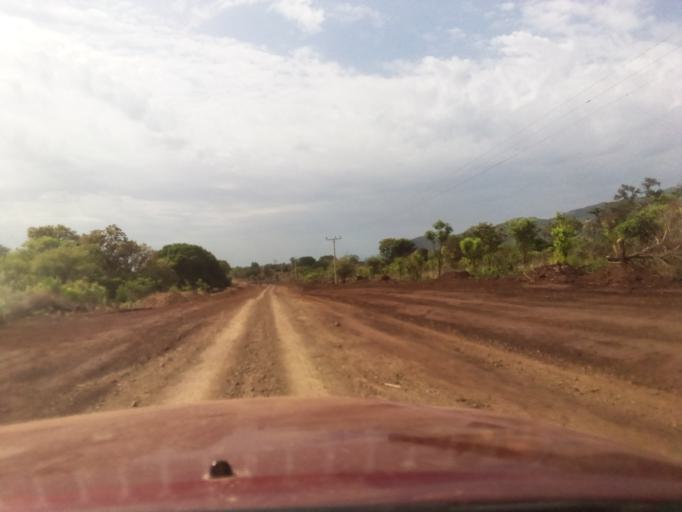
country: ET
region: Oromiya
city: Mendi
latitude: 10.0573
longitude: 35.2857
